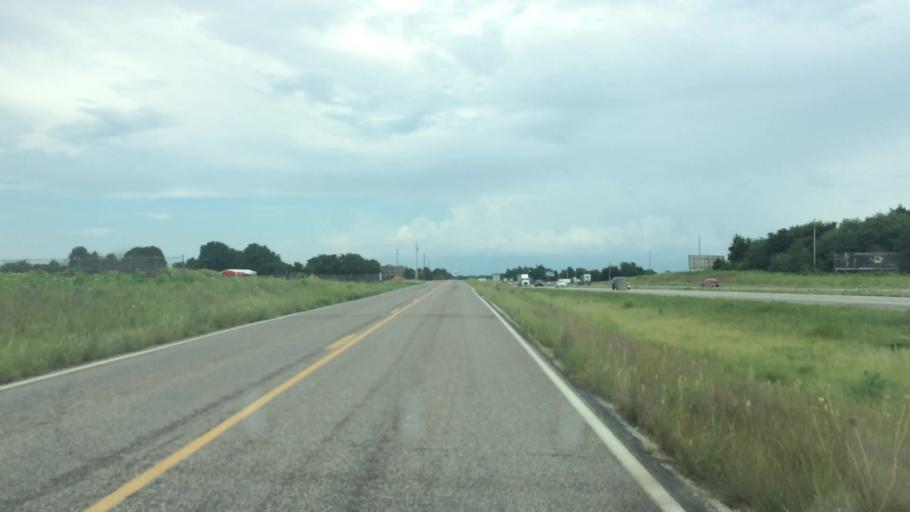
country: US
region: Missouri
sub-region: Greene County
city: Strafford
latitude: 37.2587
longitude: -93.1595
